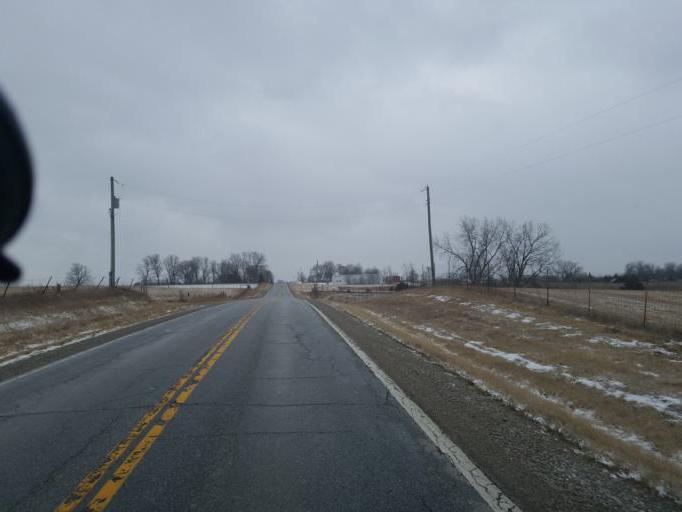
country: US
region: Missouri
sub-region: Putnam County
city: Unionville
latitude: 40.5135
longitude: -93.0094
